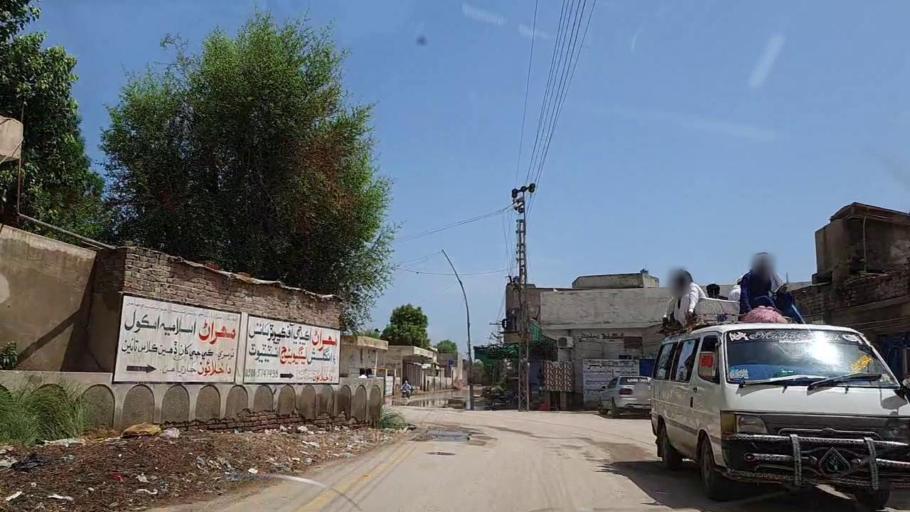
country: PK
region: Sindh
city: Naushahro Firoz
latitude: 26.8365
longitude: 68.1234
